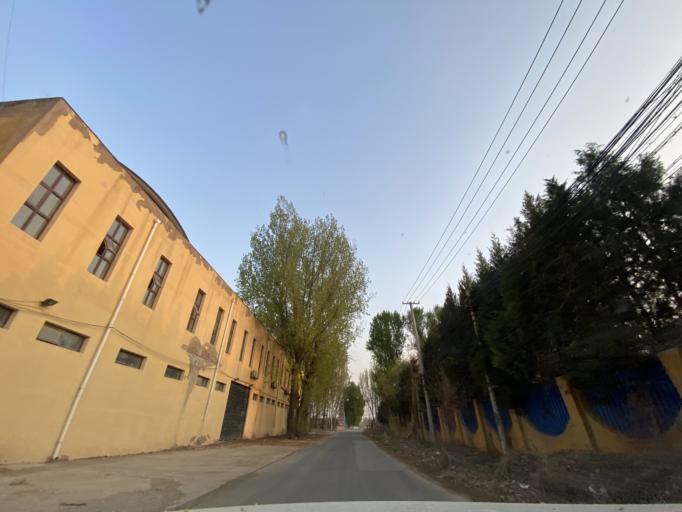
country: CN
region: Beijing
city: Weishanzhuang
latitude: 39.6076
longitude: 116.4218
